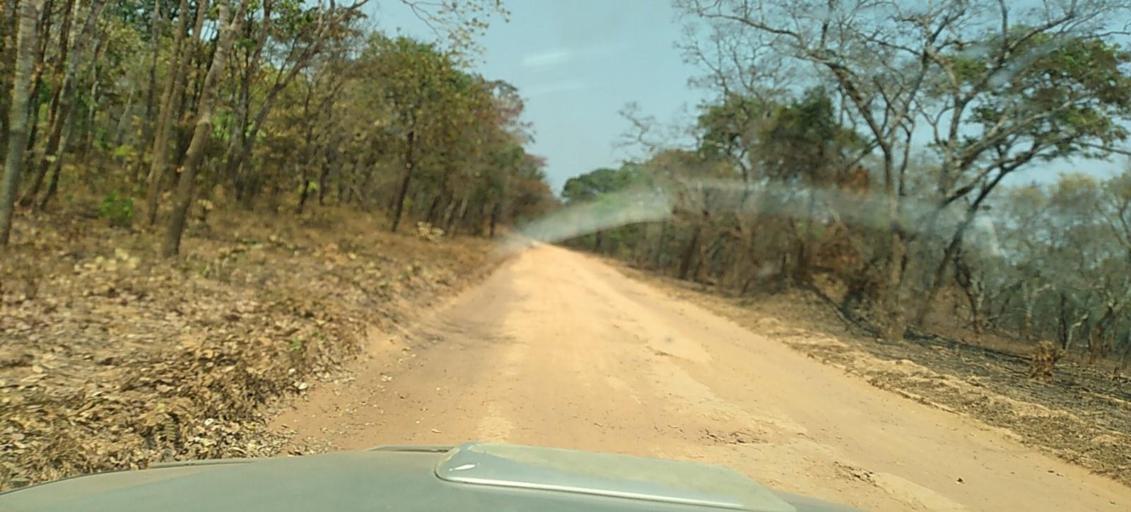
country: ZM
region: North-Western
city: Kasempa
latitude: -13.6583
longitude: 26.2647
